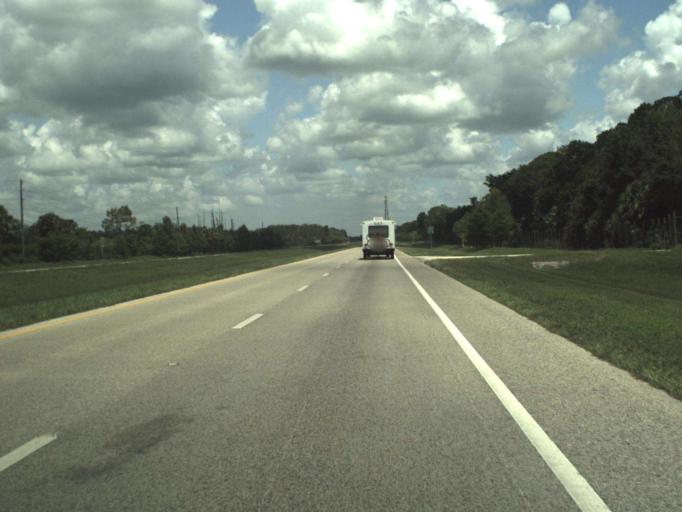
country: US
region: Florida
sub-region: Indian River County
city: Fellsmere
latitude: 27.6597
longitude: -80.7918
